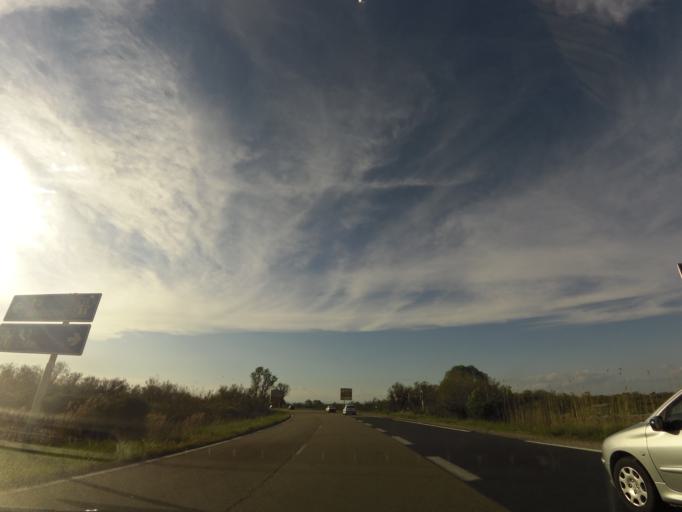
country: FR
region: Languedoc-Roussillon
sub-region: Departement de l'Herault
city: La Grande-Motte
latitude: 43.5766
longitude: 4.1033
